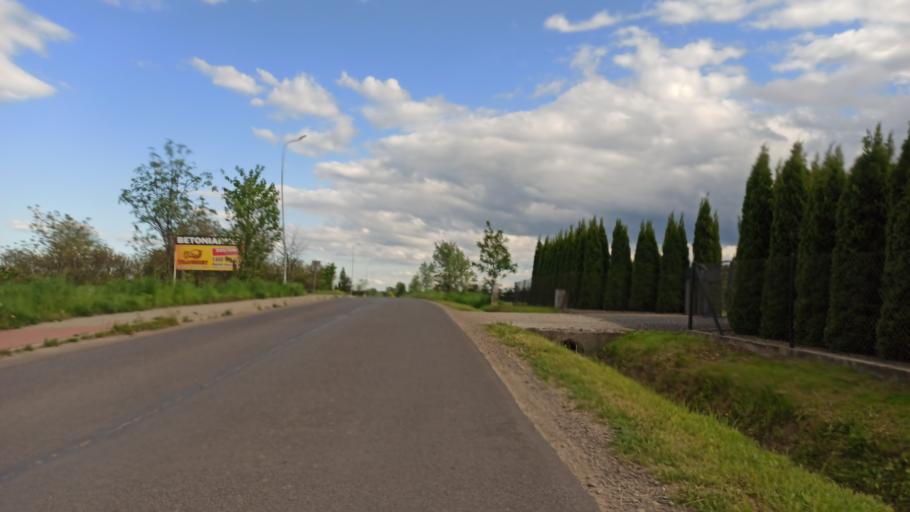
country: PL
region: Subcarpathian Voivodeship
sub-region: Powiat jaroslawski
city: Radymno
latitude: 49.9274
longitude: 22.8458
